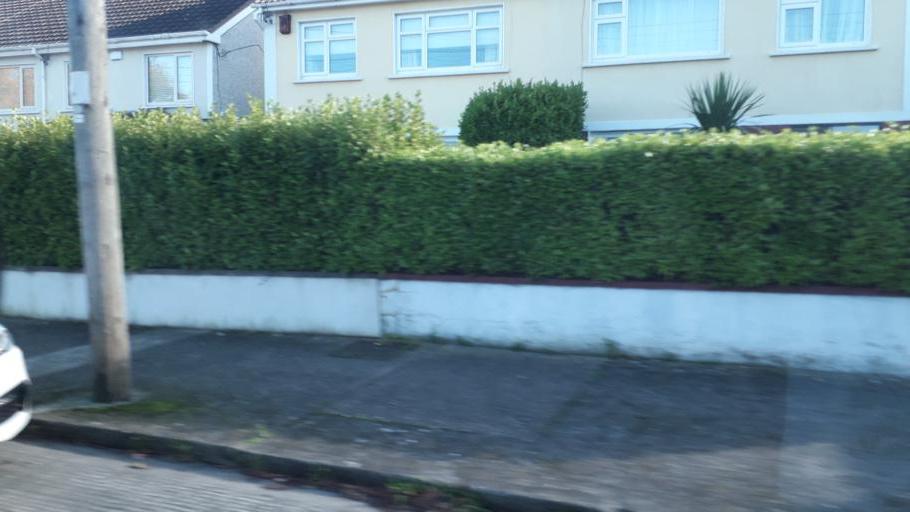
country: IE
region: Leinster
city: Donaghmede
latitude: 53.3869
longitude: -6.1628
